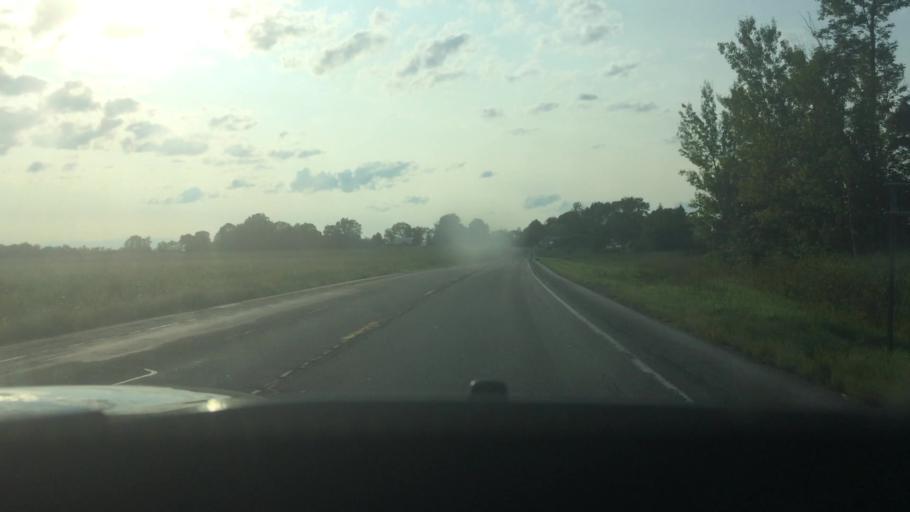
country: US
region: New York
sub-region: St. Lawrence County
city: Ogdensburg
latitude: 44.6694
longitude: -75.3791
